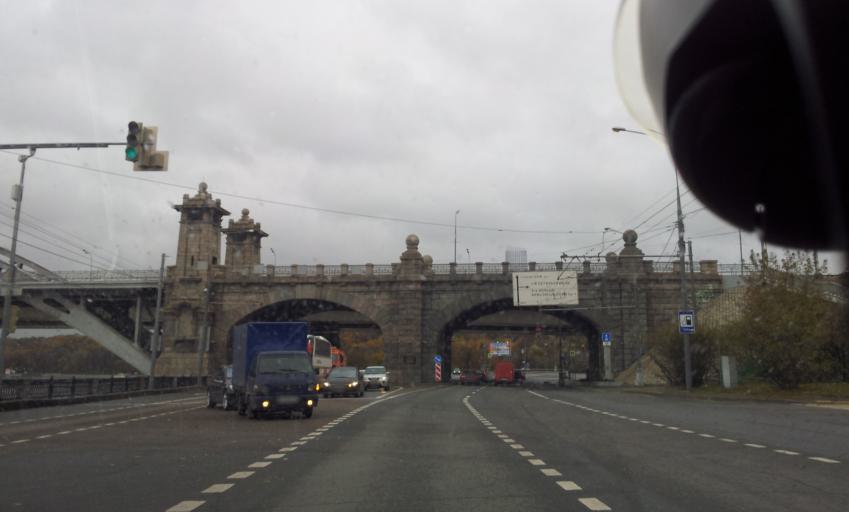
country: RU
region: Moscow
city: Luzhniki
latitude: 55.7295
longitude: 37.5487
